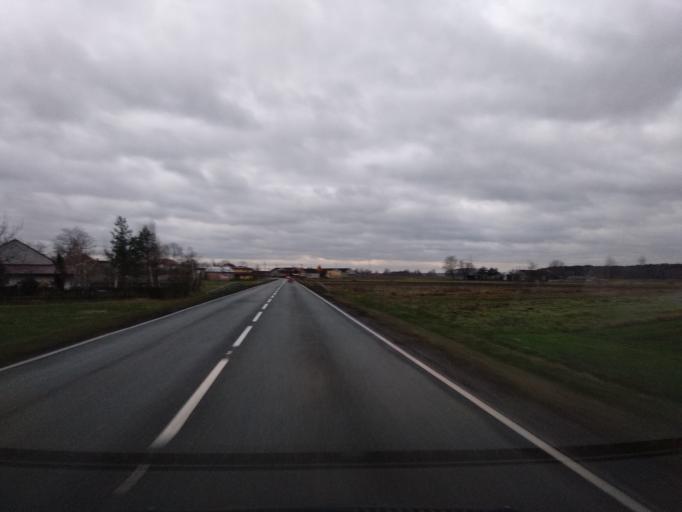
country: PL
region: Greater Poland Voivodeship
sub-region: Powiat koninski
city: Rychwal
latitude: 52.1251
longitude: 18.1740
